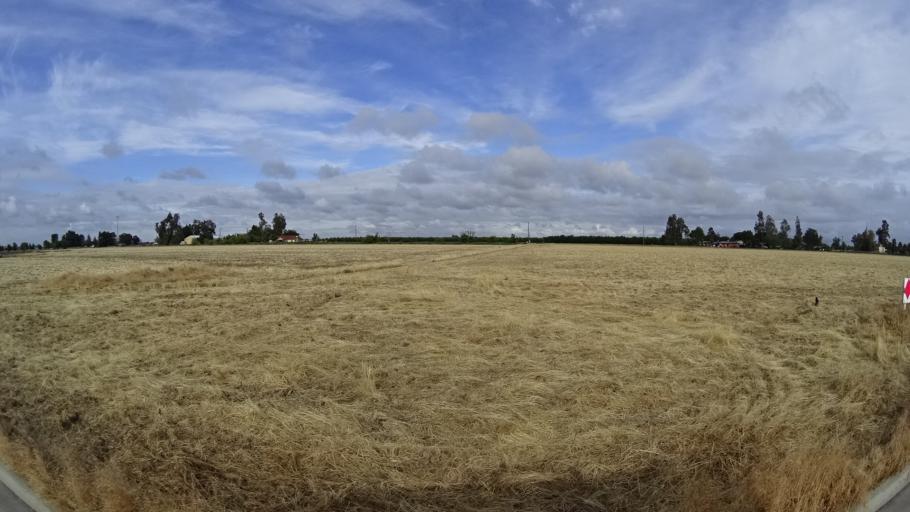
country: US
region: California
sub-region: Kings County
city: Armona
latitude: 36.3245
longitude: -119.6792
